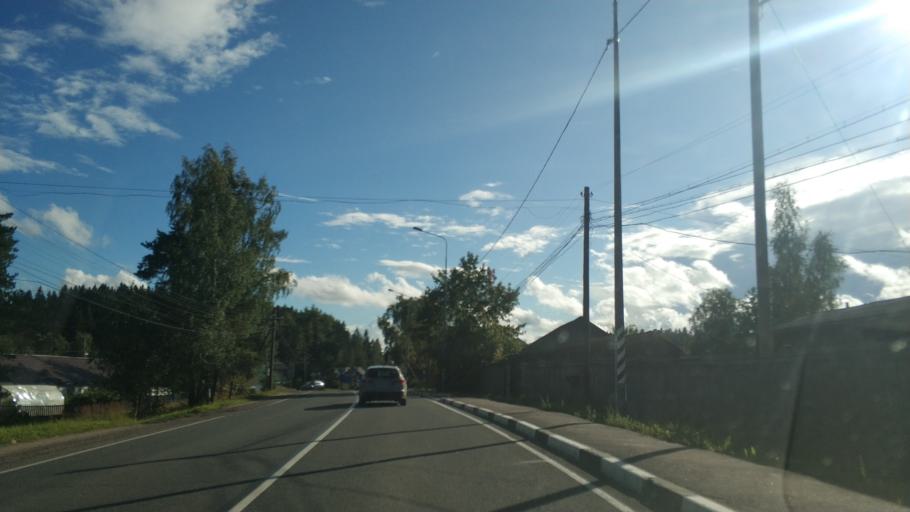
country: RU
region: Republic of Karelia
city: Lakhdenpokh'ya
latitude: 61.5286
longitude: 30.2038
